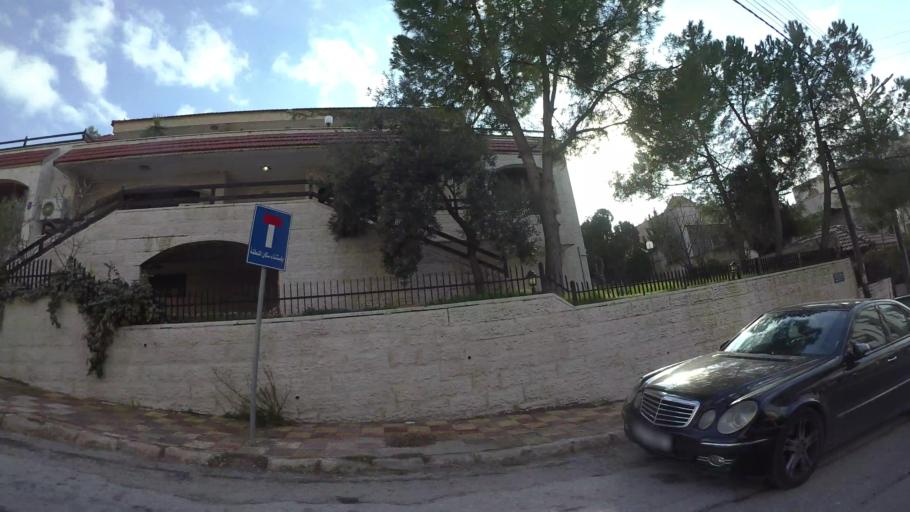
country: JO
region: Amman
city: Al Jubayhah
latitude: 31.9857
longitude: 35.8767
